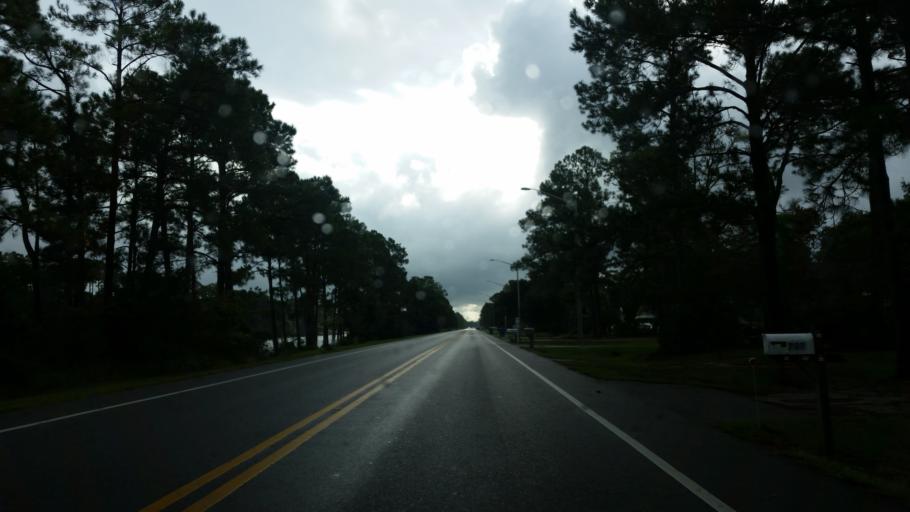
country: US
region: Alabama
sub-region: Baldwin County
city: Gulf Shores
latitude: 30.2791
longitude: -87.6749
